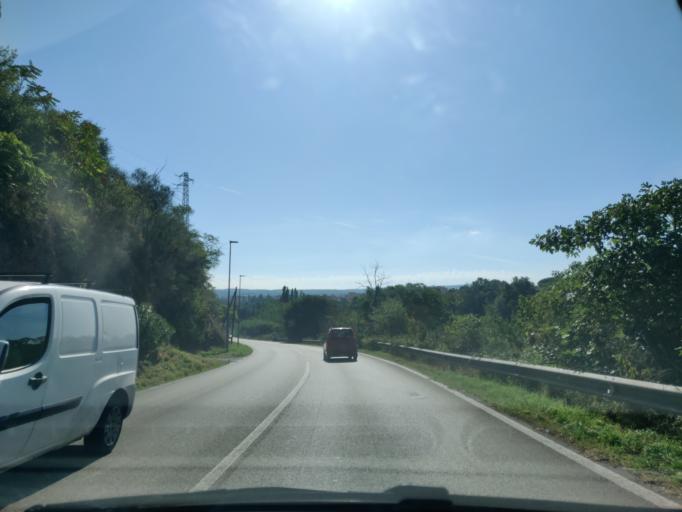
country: IT
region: Latium
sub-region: Provincia di Viterbo
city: Viterbo
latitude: 42.4162
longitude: 12.0912
